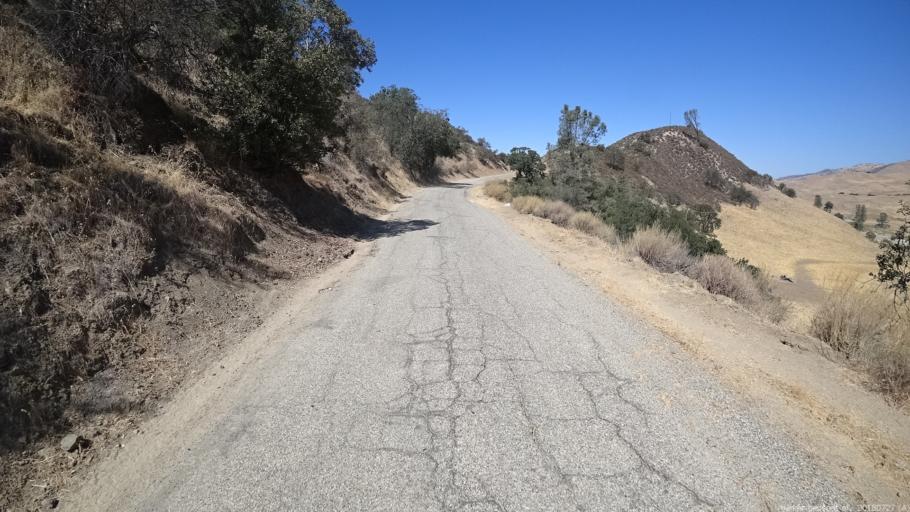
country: US
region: California
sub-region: Monterey County
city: King City
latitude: 36.2944
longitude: -120.8958
